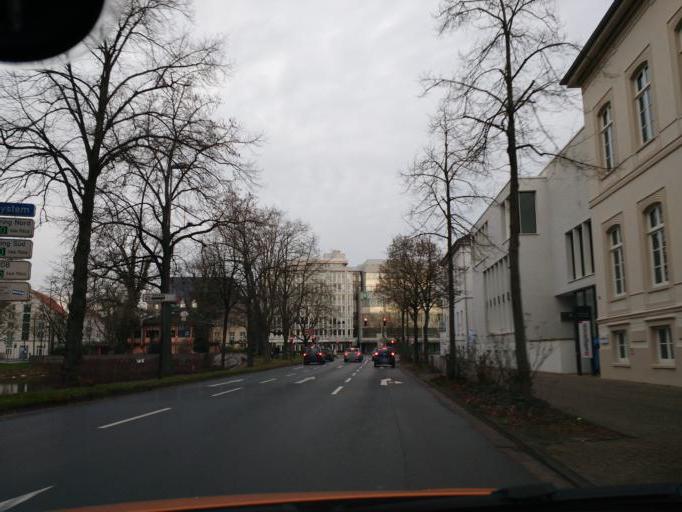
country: DE
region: Lower Saxony
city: Oldenburg
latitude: 53.1393
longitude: 8.2188
